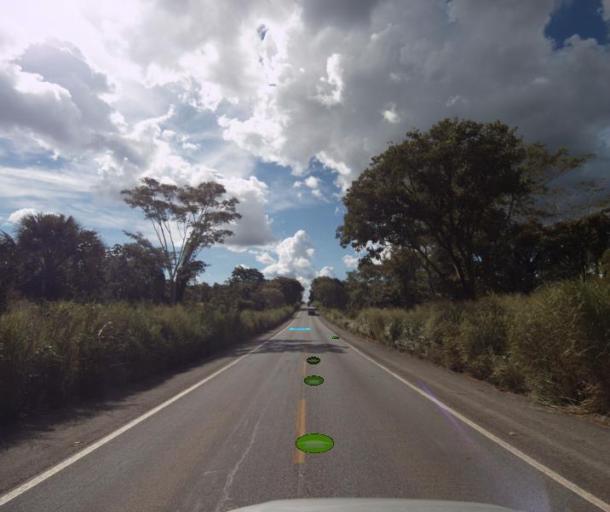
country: BR
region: Goias
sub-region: Porangatu
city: Porangatu
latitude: -13.1618
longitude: -49.1778
